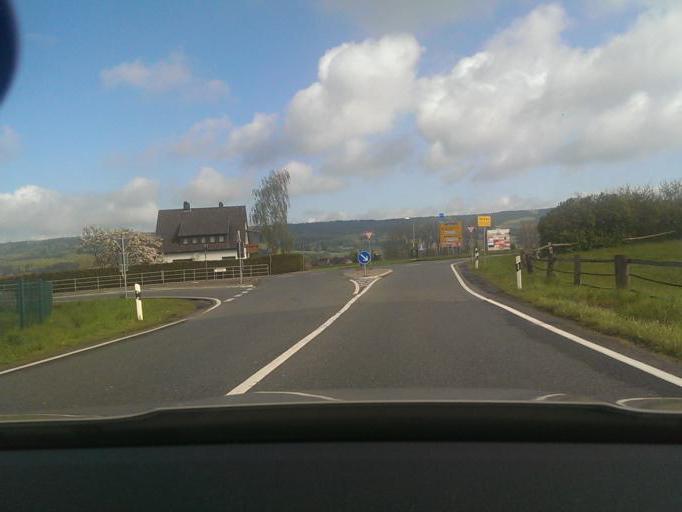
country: DE
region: Lower Saxony
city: Rehren
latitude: 52.2343
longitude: 9.2409
